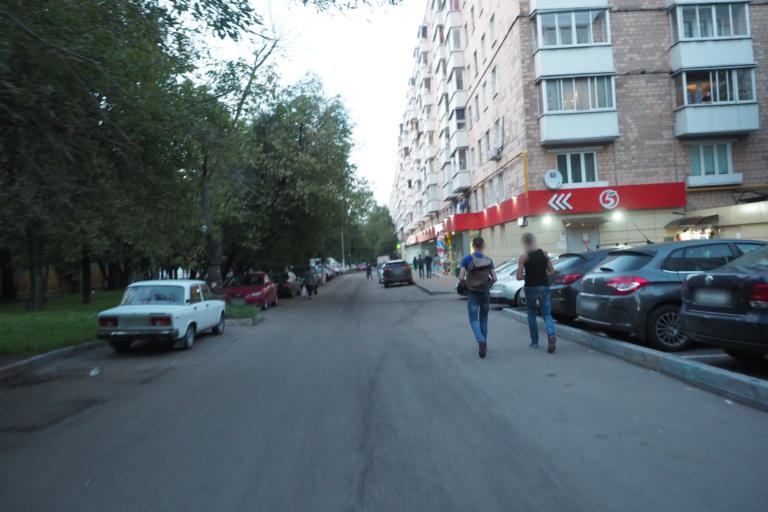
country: RU
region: Moskovskaya
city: Kozhukhovo
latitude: 55.6815
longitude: 37.6667
